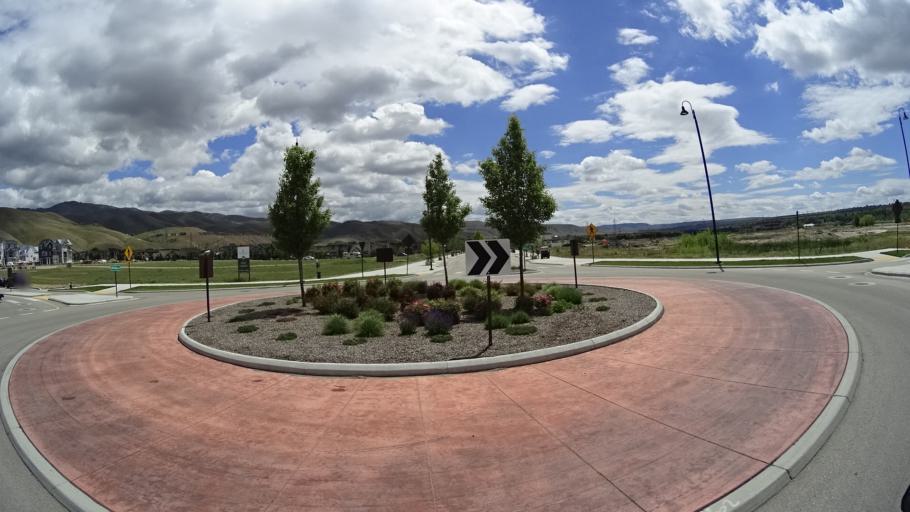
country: US
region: Idaho
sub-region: Ada County
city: Boise
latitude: 43.5743
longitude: -116.1339
